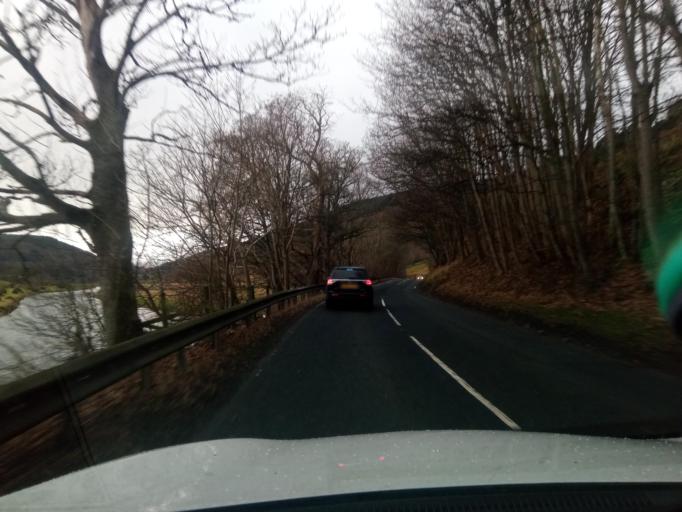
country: GB
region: Scotland
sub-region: The Scottish Borders
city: Innerleithen
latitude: 55.6296
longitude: -2.9858
